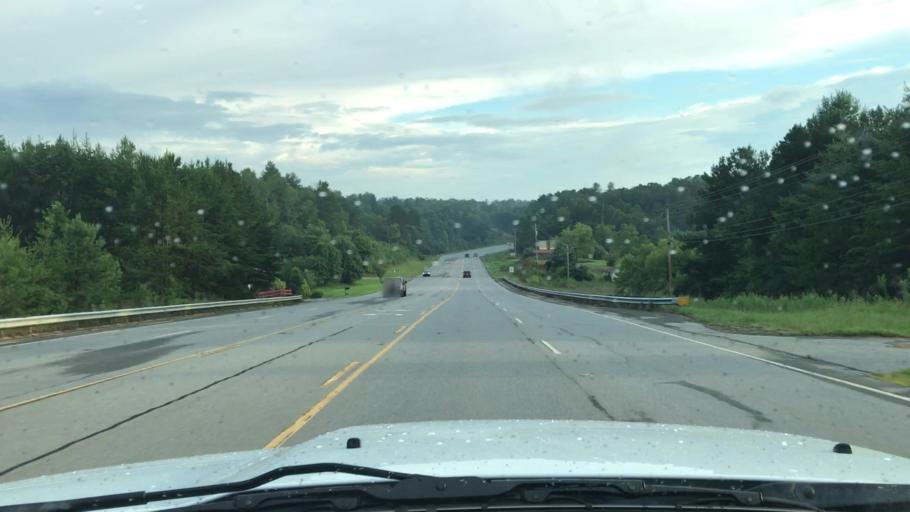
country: US
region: North Carolina
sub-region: Cherokee County
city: Murphy
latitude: 35.0179
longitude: -84.1211
